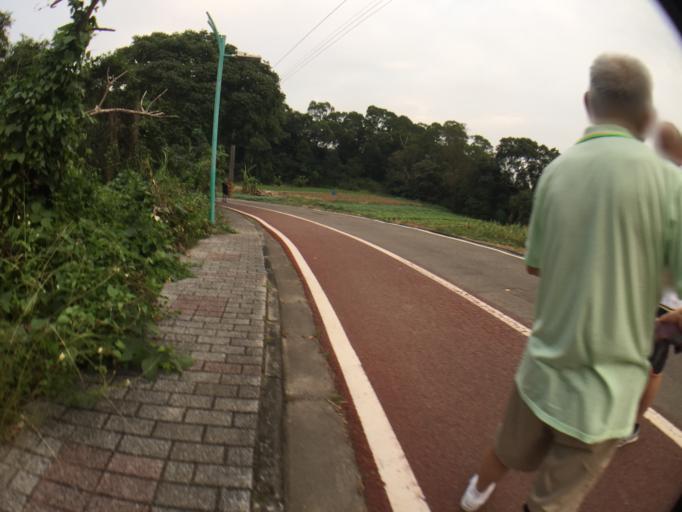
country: TW
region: Taiwan
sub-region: Hsinchu
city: Hsinchu
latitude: 24.7721
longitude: 120.9764
